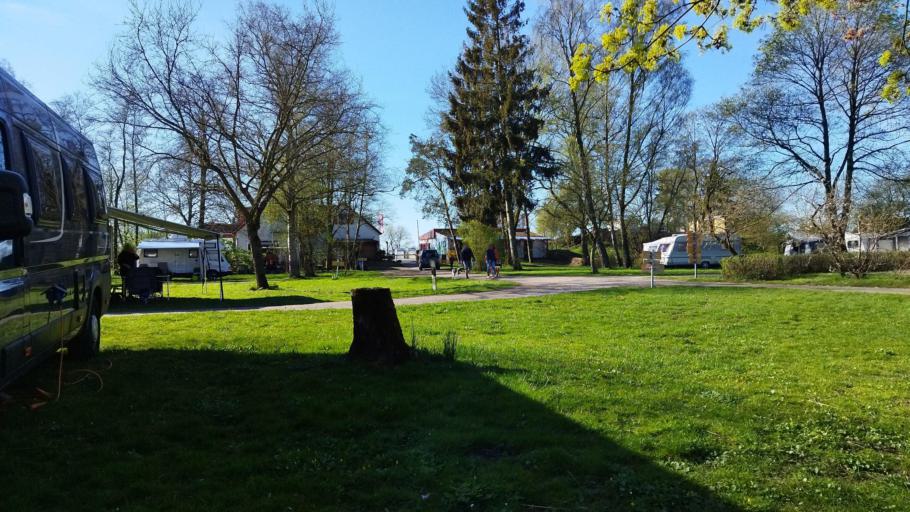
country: DE
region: Lower Saxony
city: Neuenkirchen
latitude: 53.1971
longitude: 8.5110
